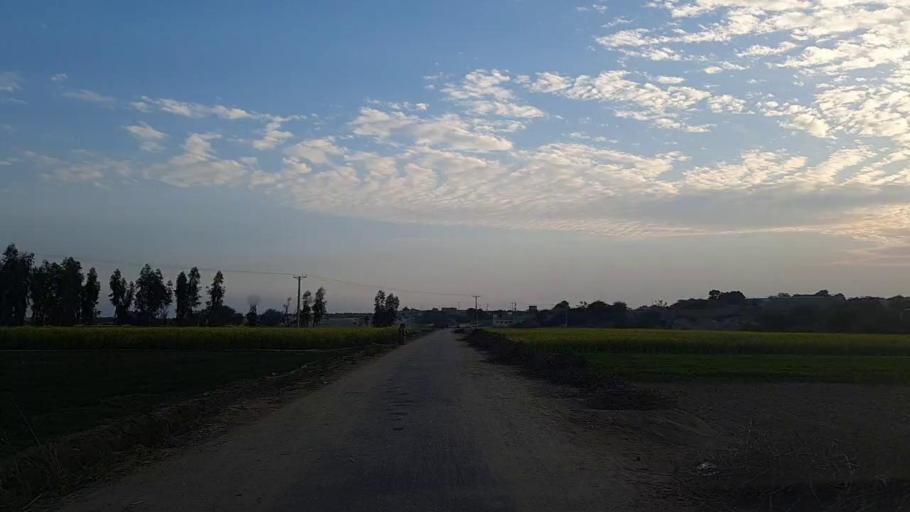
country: PK
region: Sindh
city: Daur
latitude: 26.4149
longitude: 68.4678
